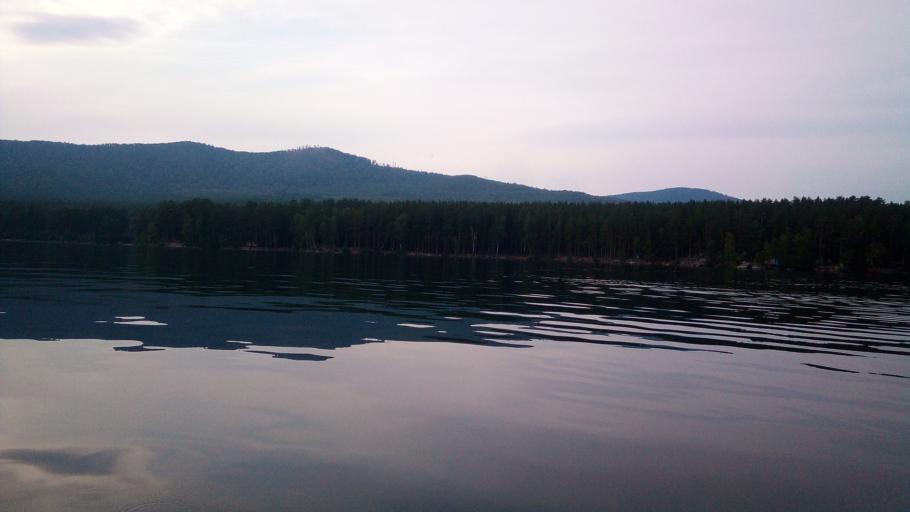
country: RU
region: Chelyabinsk
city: Turgoyak
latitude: 55.1749
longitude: 60.0297
